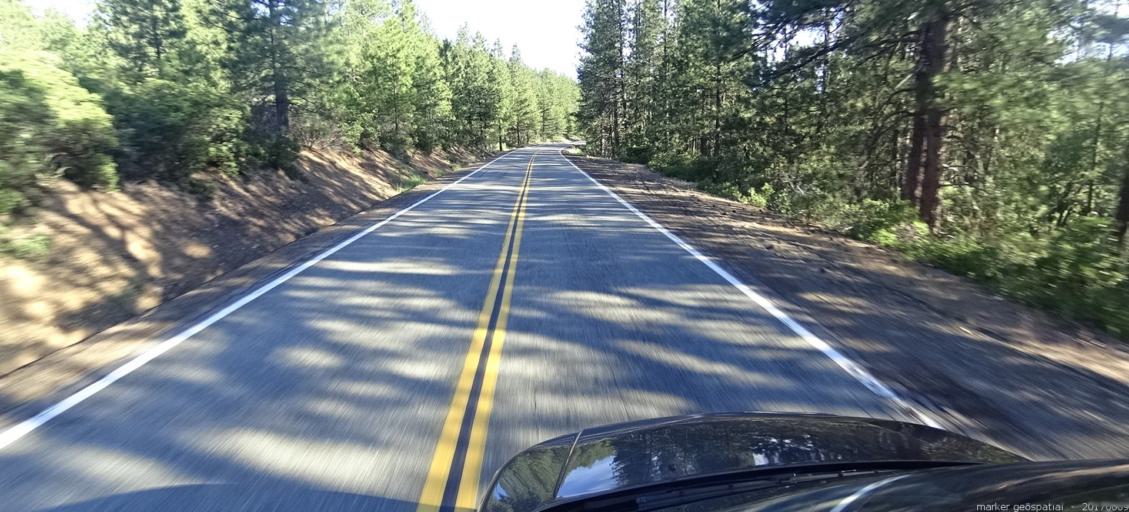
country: US
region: California
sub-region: Siskiyou County
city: Weed
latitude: 41.4292
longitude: -122.6375
